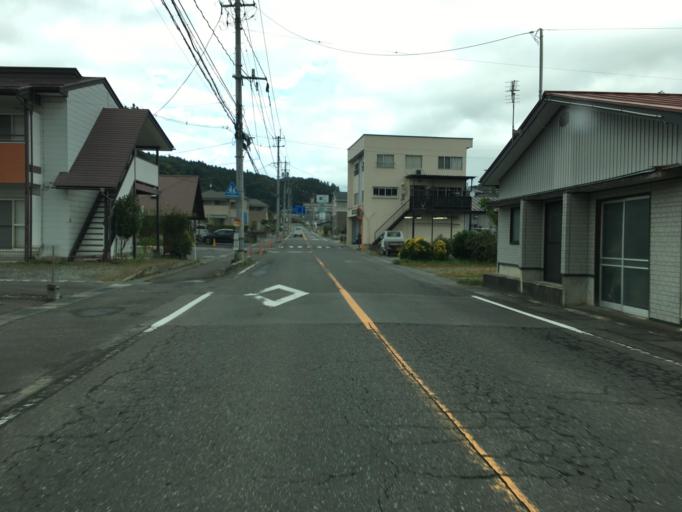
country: JP
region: Fukushima
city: Nihommatsu
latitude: 37.6024
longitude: 140.4442
